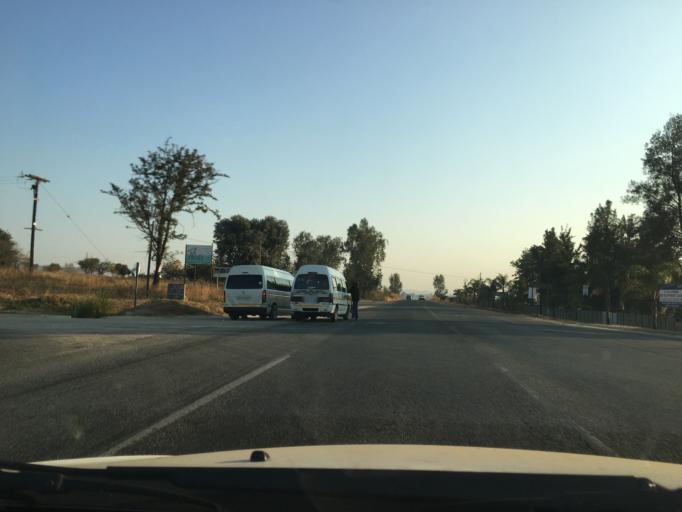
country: ZA
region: Gauteng
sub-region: West Rand District Municipality
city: Muldersdriseloop
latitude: -26.0143
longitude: 27.8589
